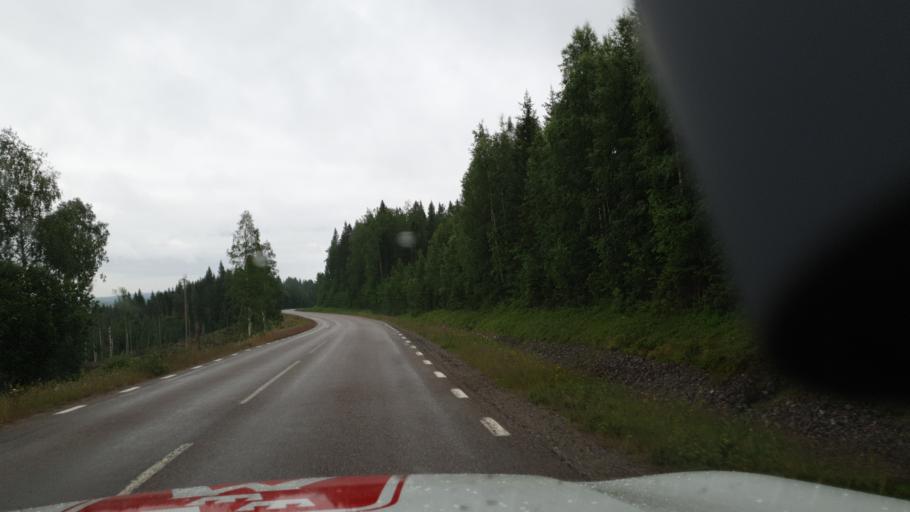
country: SE
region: Vaesterbotten
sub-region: Vannas Kommun
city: Vaennaes
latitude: 63.7921
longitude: 19.8165
